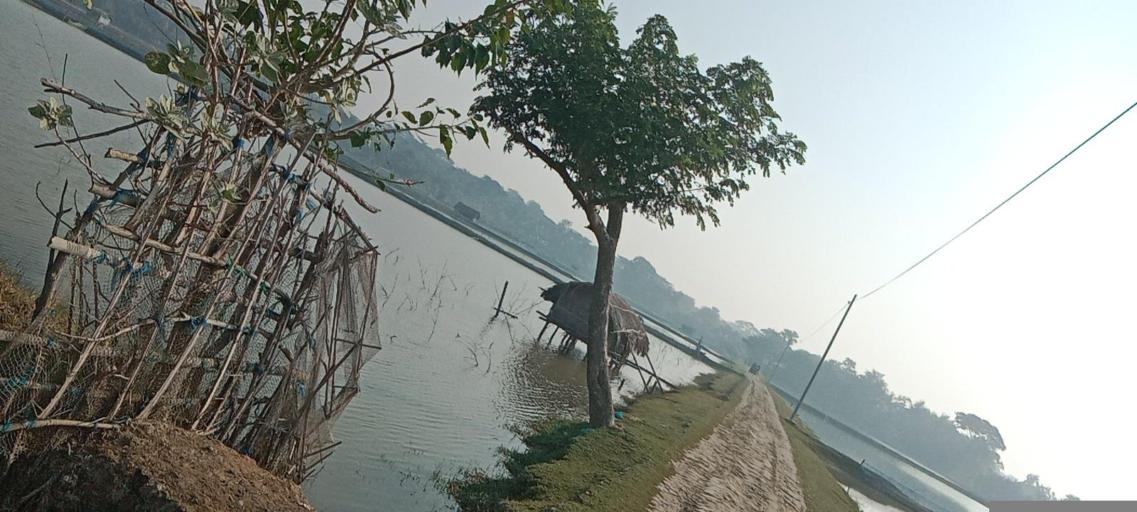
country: BD
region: Khulna
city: Phultala
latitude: 22.6098
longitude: 89.5855
